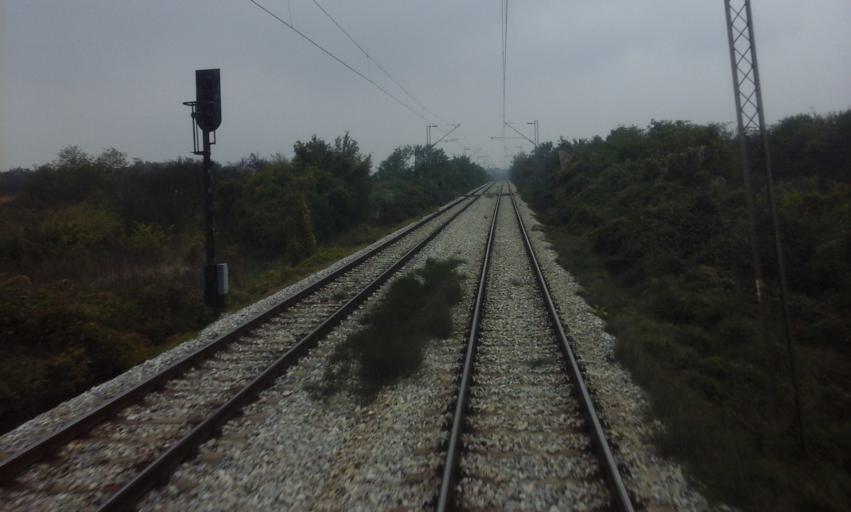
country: RS
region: Central Serbia
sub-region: Sumadijski Okrug
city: Lapovo
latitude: 44.2167
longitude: 21.0946
